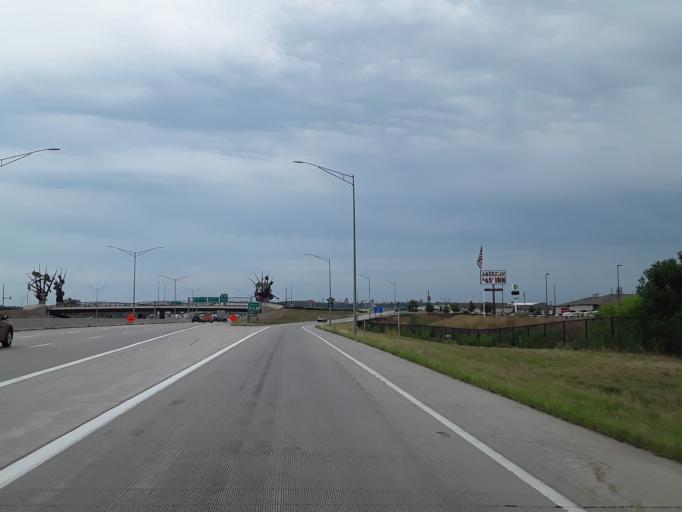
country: US
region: Iowa
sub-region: Pottawattamie County
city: Council Bluffs
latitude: 41.2327
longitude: -95.8742
